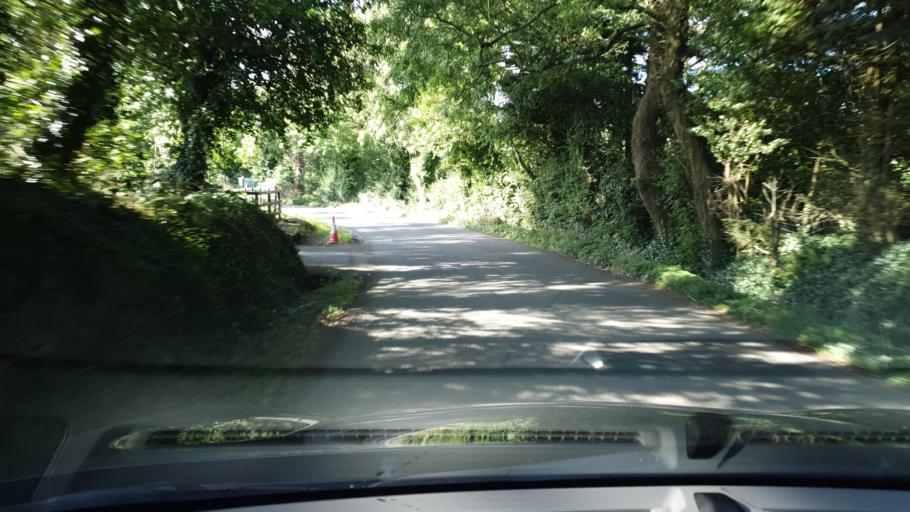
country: IE
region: Leinster
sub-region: An Mhi
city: Ashbourne
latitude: 53.5482
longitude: -6.3593
